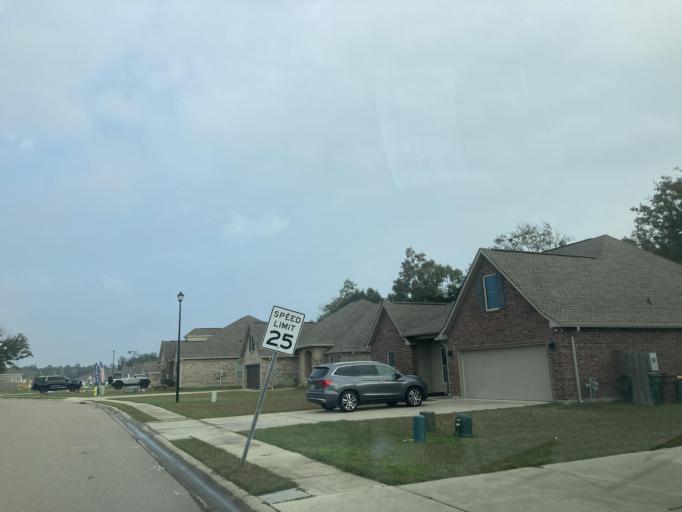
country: US
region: Mississippi
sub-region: Harrison County
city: Long Beach
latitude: 30.3711
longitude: -89.1581
